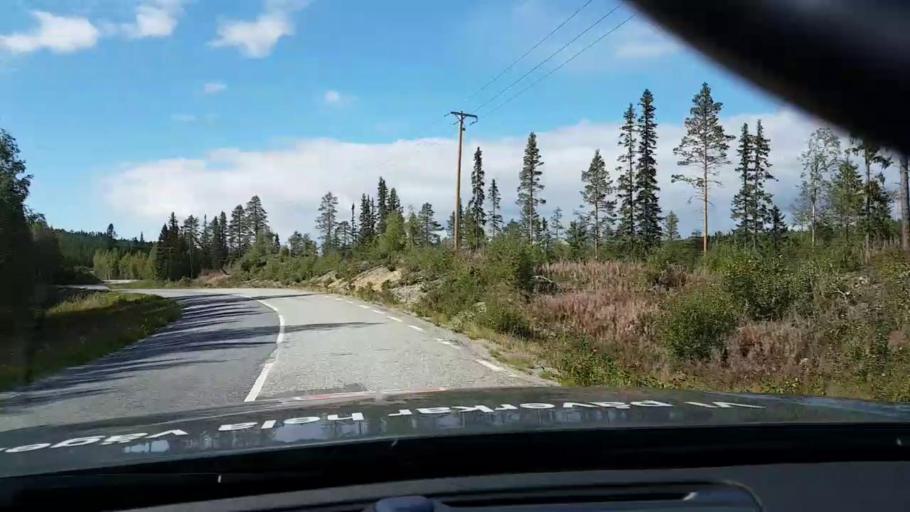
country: SE
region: Vaesterbotten
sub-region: Asele Kommun
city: Asele
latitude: 63.8280
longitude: 17.4712
